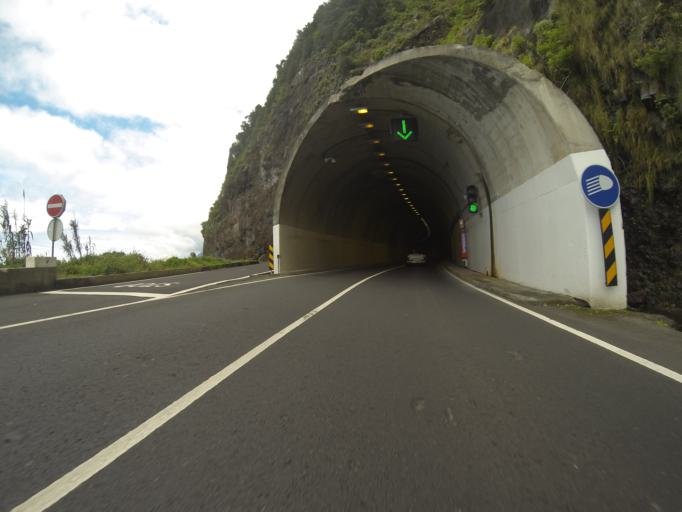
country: PT
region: Madeira
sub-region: Sao Vicente
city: Sao Vicente
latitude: 32.8142
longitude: -17.0775
